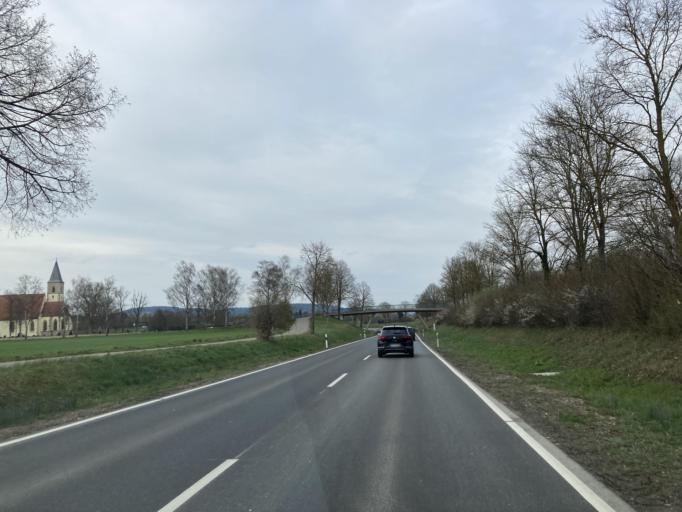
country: DE
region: Baden-Wuerttemberg
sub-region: Tuebingen Region
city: Rottenburg
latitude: 48.4831
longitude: 8.9504
